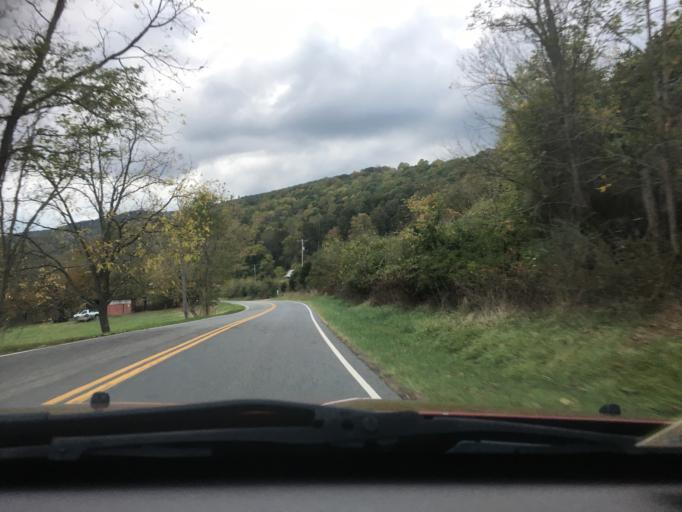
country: US
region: Virginia
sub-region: Giles County
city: Pearisburg
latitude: 37.2115
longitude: -80.7725
